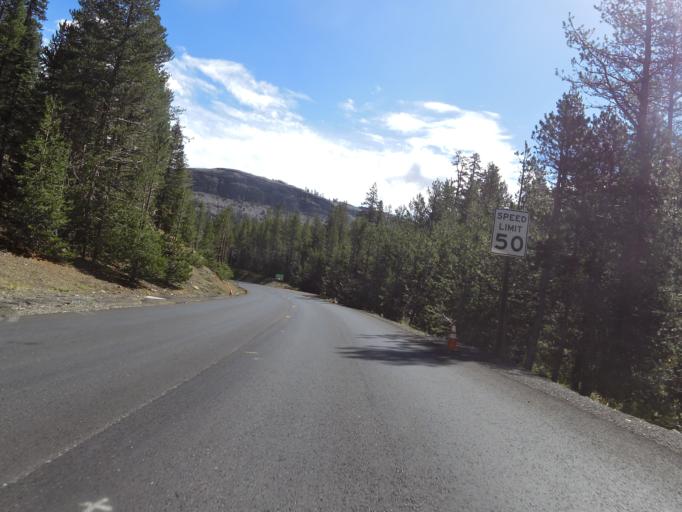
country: US
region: California
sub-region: El Dorado County
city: South Lake Tahoe
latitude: 38.7003
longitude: -120.0828
